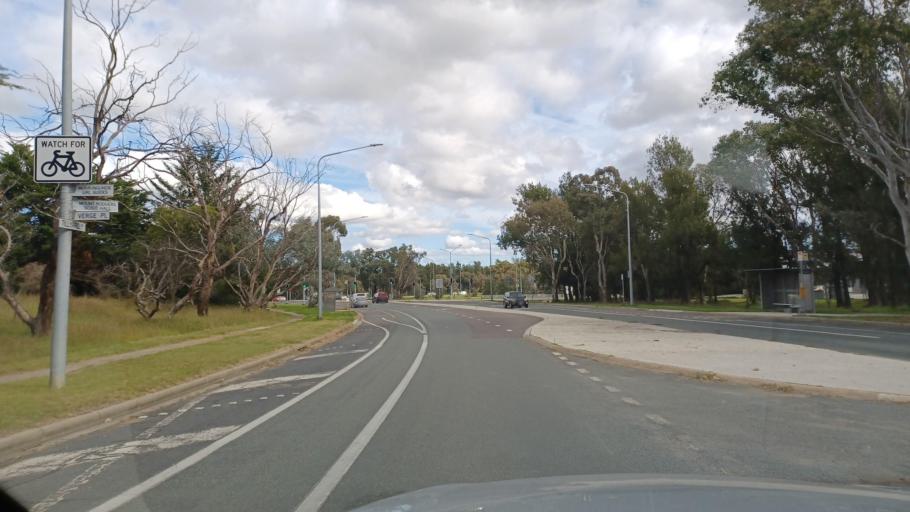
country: AU
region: Australian Capital Territory
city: Belconnen
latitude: -35.2055
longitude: 149.0357
